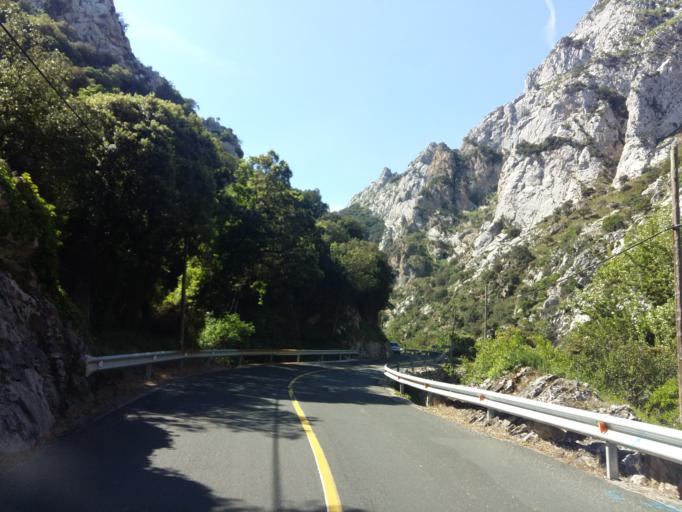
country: ES
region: Cantabria
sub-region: Provincia de Cantabria
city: Potes
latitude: 43.2082
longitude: -4.5944
